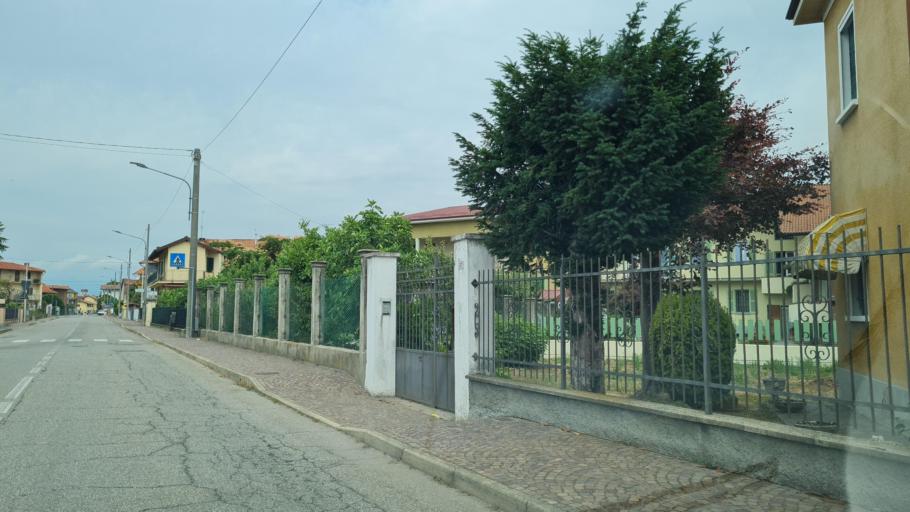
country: IT
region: Piedmont
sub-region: Provincia di Novara
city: Carpignano Sesia
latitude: 45.5309
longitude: 8.4234
